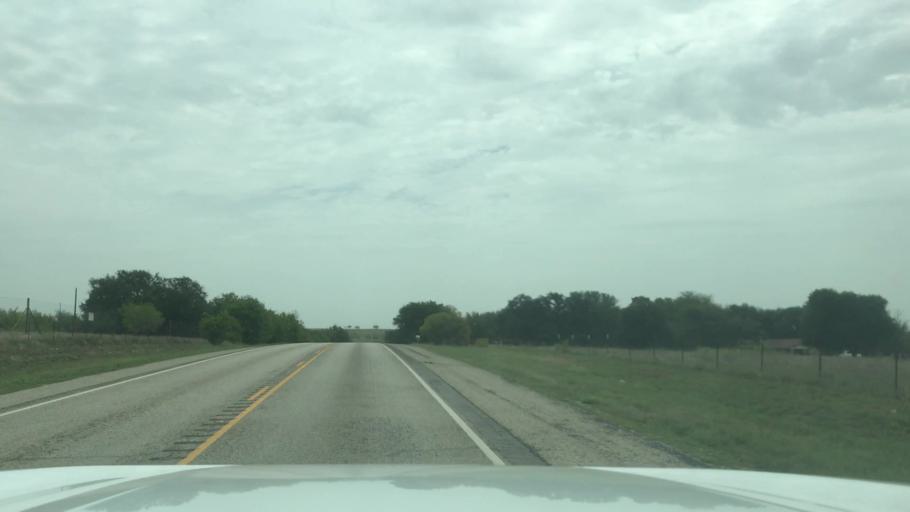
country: US
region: Texas
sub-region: Erath County
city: Dublin
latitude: 32.0576
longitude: -98.1936
